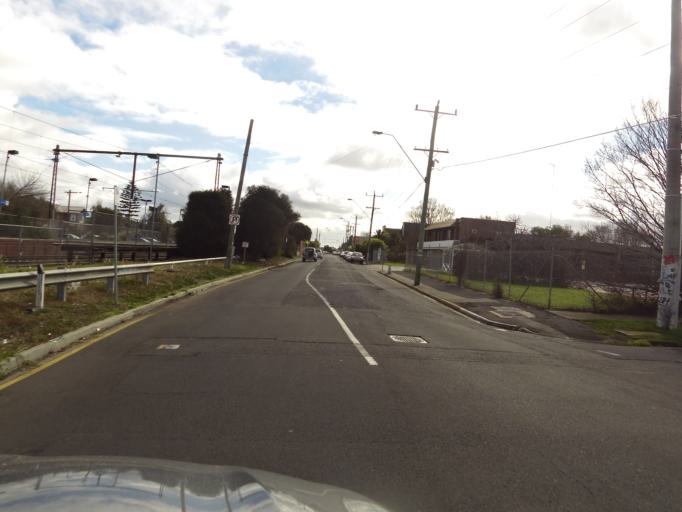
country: AU
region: Victoria
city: Spotswood
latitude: -37.8317
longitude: 144.8858
